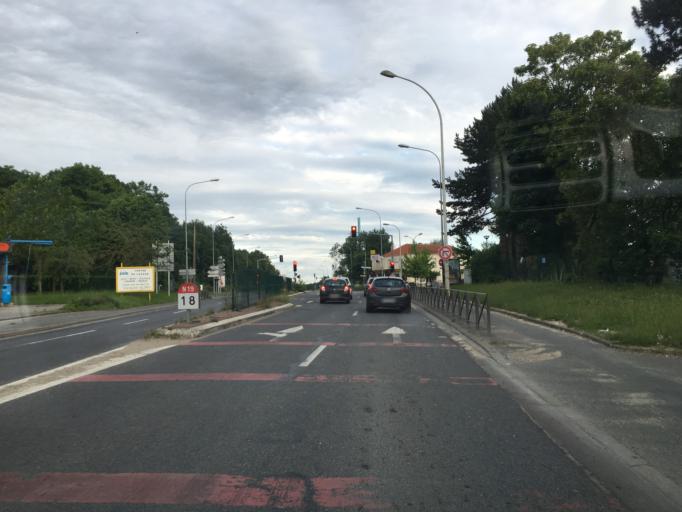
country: FR
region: Ile-de-France
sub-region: Departement du Val-de-Marne
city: Boissy-Saint-Leger
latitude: 48.7455
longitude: 2.5111
